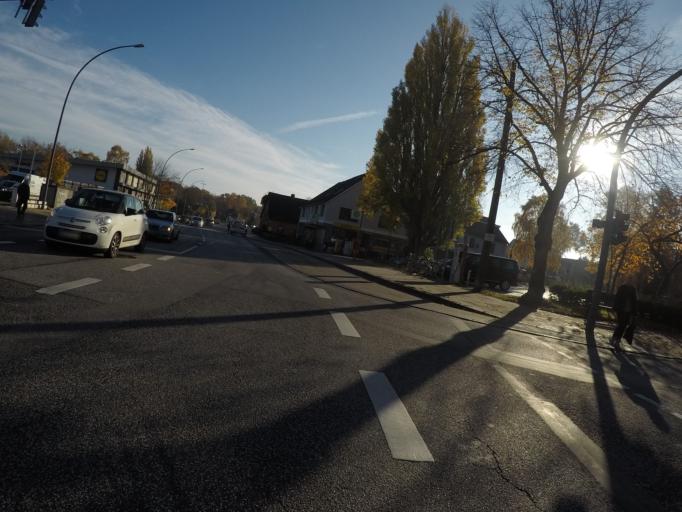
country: DE
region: Hamburg
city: Eidelstedt
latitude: 53.6294
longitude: 9.9287
